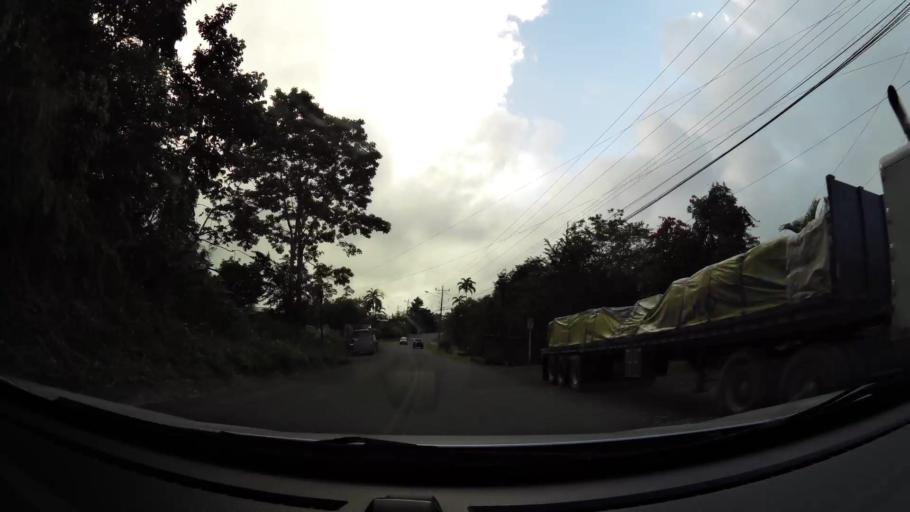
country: CR
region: Cartago
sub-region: Canton de Turrialba
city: La Suiza
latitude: 9.9567
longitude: -83.5692
